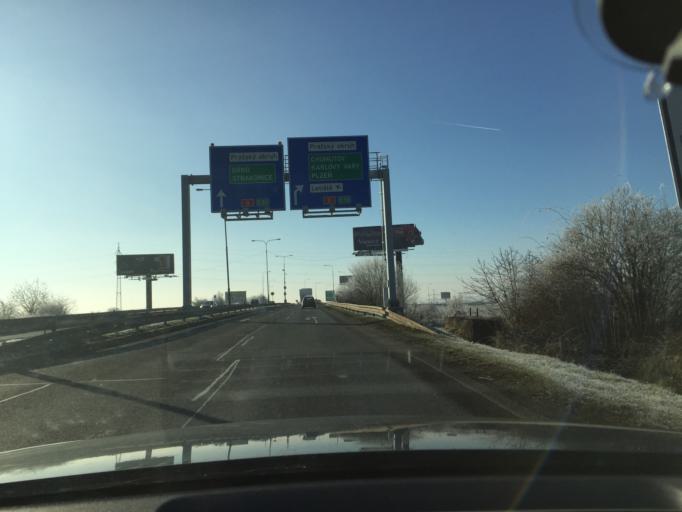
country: CZ
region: Central Bohemia
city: Cernosice
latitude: 50.0173
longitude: 14.3447
